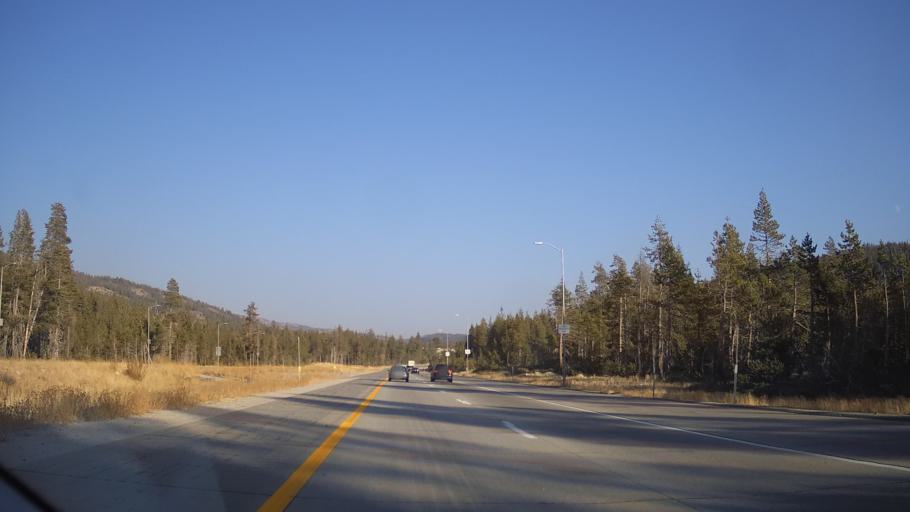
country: US
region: California
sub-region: Nevada County
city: Truckee
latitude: 39.3129
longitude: -120.4818
